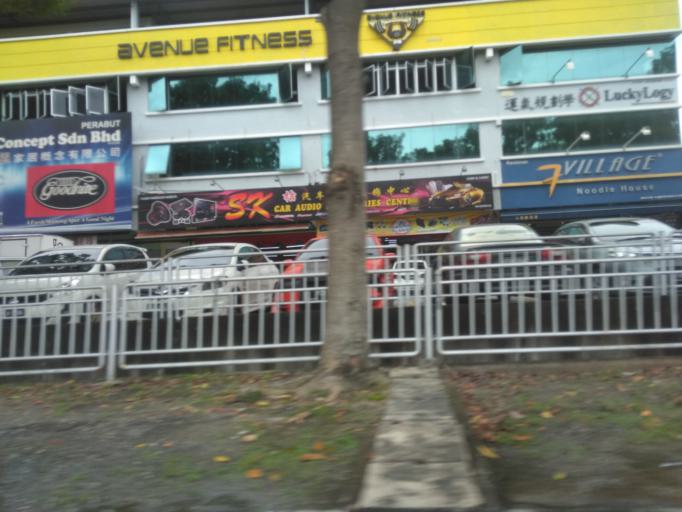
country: MY
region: Penang
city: Bukit Mertajam
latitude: 5.3364
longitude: 100.4832
